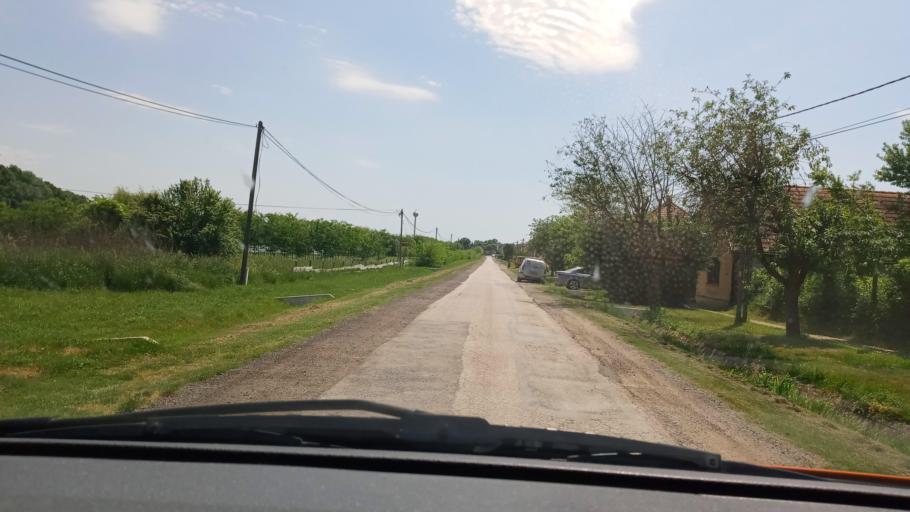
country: HU
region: Baranya
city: Harkany
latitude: 45.8348
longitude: 18.1358
